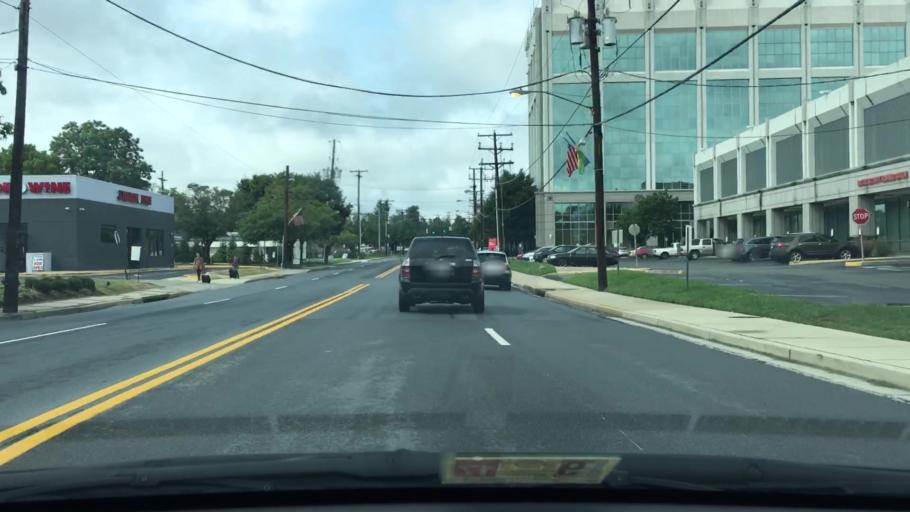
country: US
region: Maryland
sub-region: Montgomery County
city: Rockville
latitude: 39.0888
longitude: -77.1537
